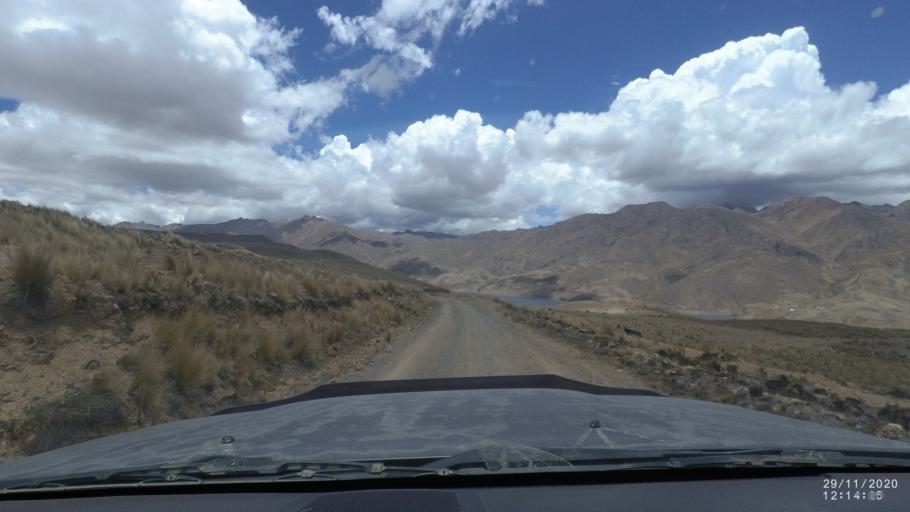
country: BO
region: Cochabamba
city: Cochabamba
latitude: -17.1086
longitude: -66.3119
